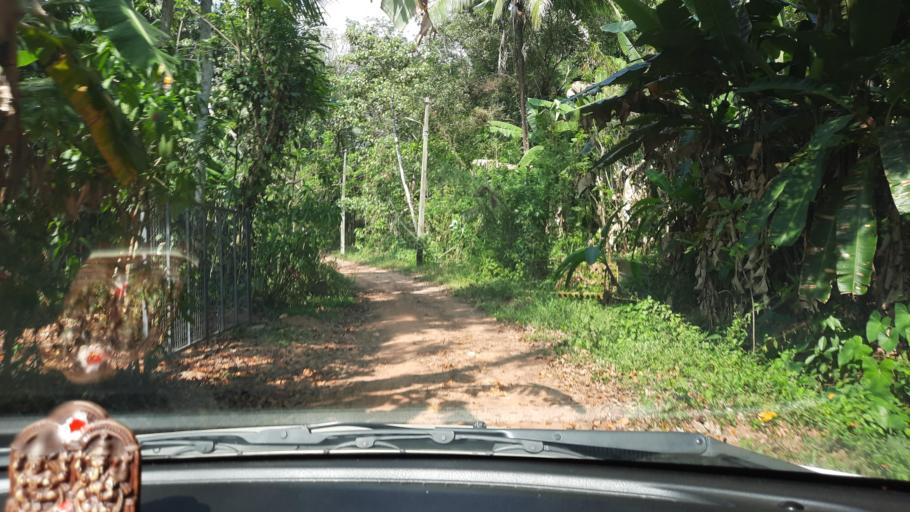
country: IN
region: Kerala
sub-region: Thiruvananthapuram
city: Nedumangad
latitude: 8.5931
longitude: 76.9258
